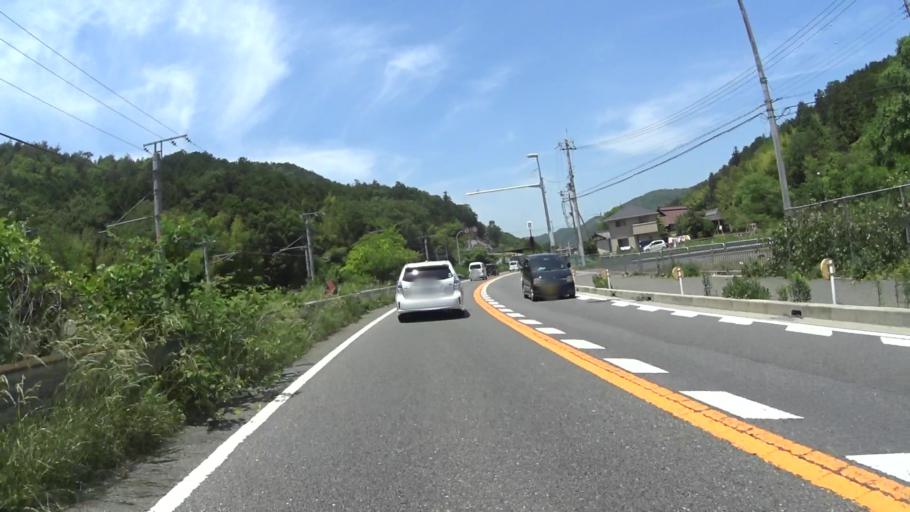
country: JP
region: Kyoto
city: Kameoka
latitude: 35.0831
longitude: 135.5049
